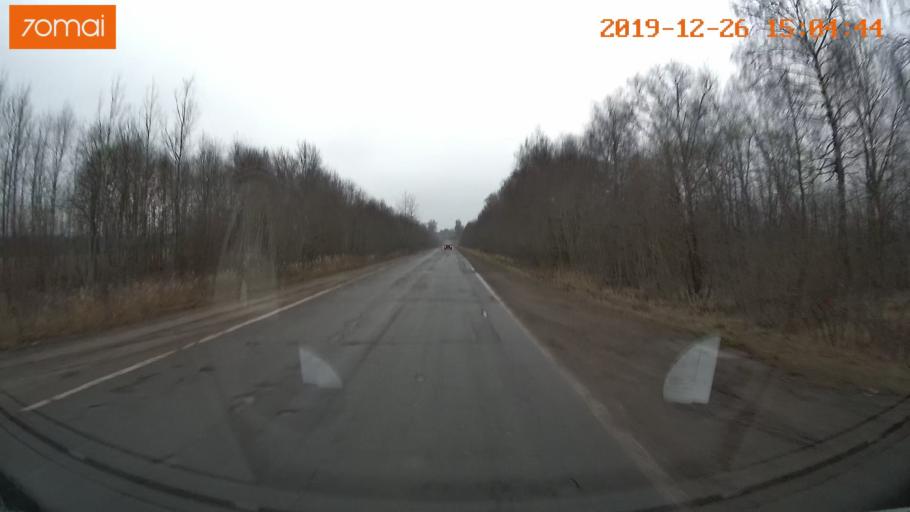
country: RU
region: Jaroslavl
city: Rybinsk
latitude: 58.1966
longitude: 38.8586
